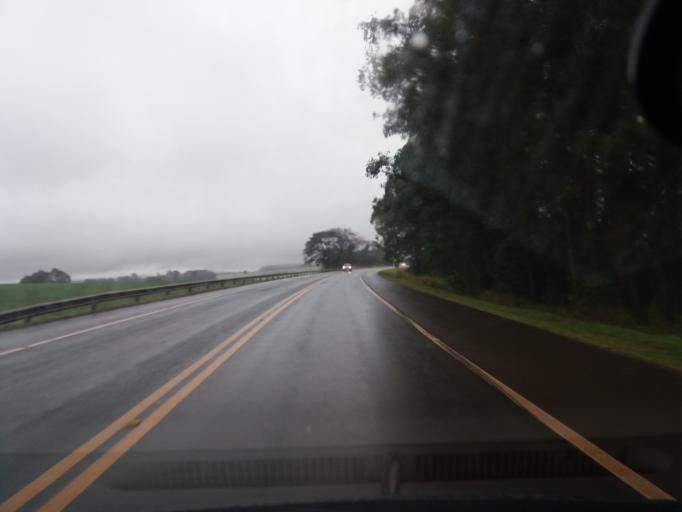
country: BR
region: Parana
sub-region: Campo Mourao
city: Campo Mourao
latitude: -24.3069
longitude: -52.6081
